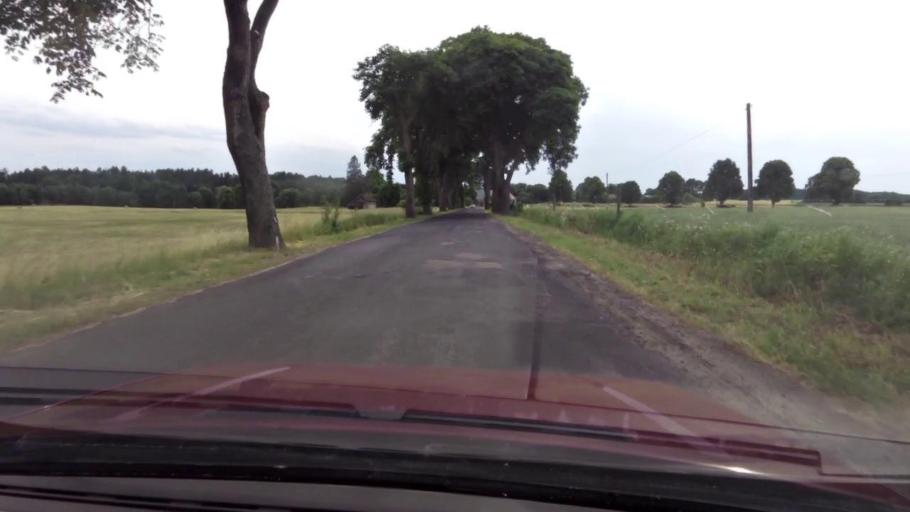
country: PL
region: Pomeranian Voivodeship
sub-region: Powiat bytowski
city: Trzebielino
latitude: 54.2664
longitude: 17.0664
